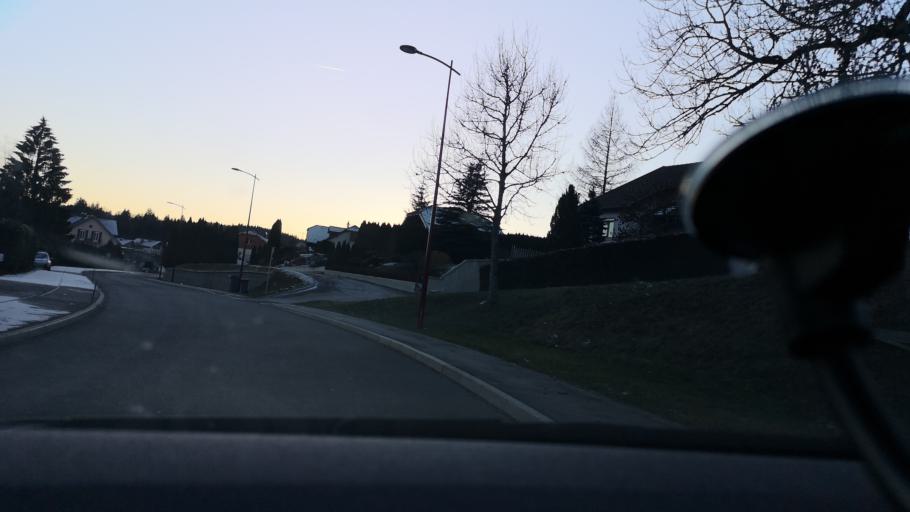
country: FR
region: Franche-Comte
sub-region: Departement du Doubs
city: Pontarlier
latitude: 46.8574
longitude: 6.3379
